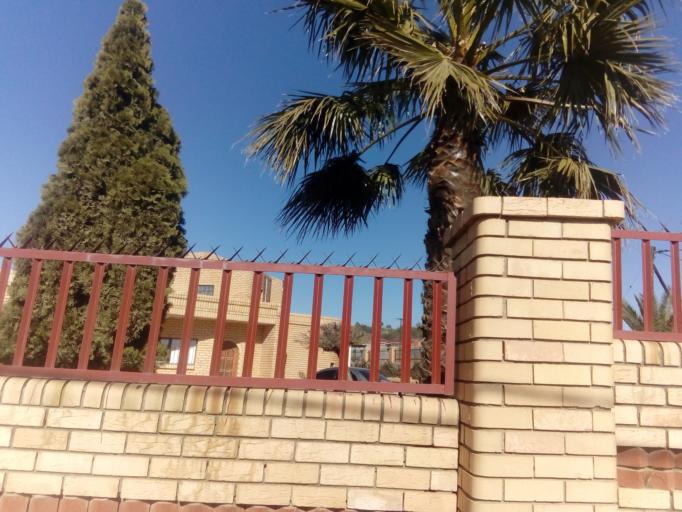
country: LS
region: Berea
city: Teyateyaneng
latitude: -29.1426
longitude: 27.7646
